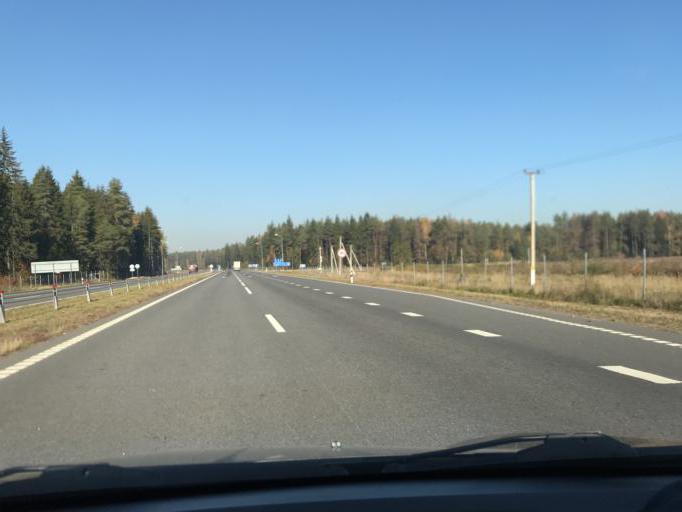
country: BY
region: Mogilev
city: Kirawsk
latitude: 53.2167
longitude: 29.3421
